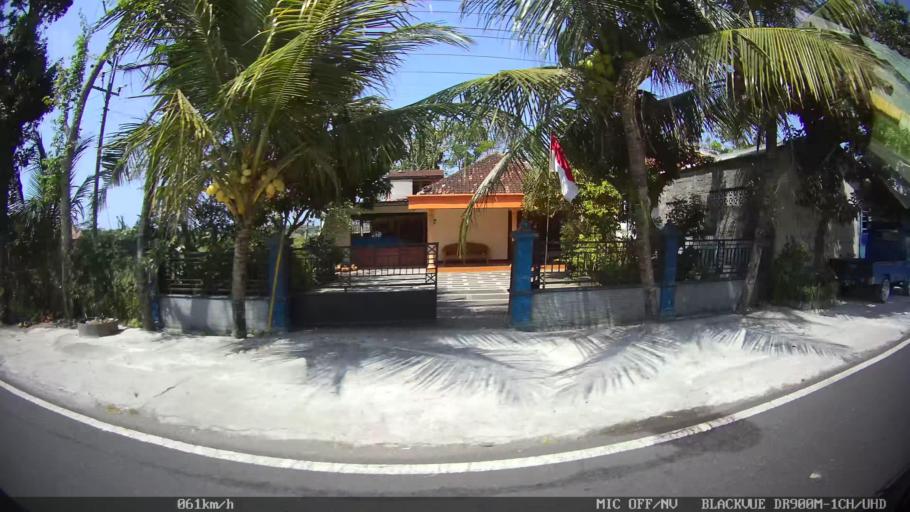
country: ID
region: Daerah Istimewa Yogyakarta
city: Srandakan
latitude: -7.8912
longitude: 110.1212
